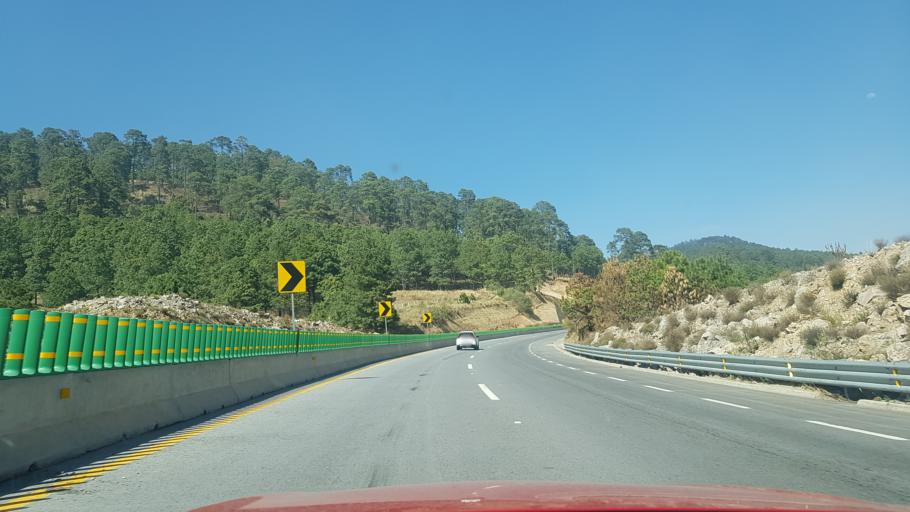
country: MX
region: Mexico
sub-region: Lerma
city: Santa Cruz Huitzizilapan
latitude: 19.3811
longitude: -99.4193
